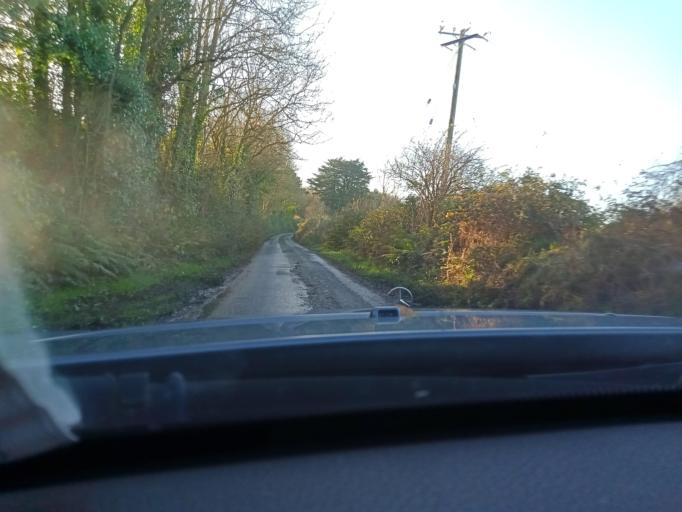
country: IE
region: Leinster
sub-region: Kilkenny
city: Mooncoin
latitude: 52.2930
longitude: -7.1828
